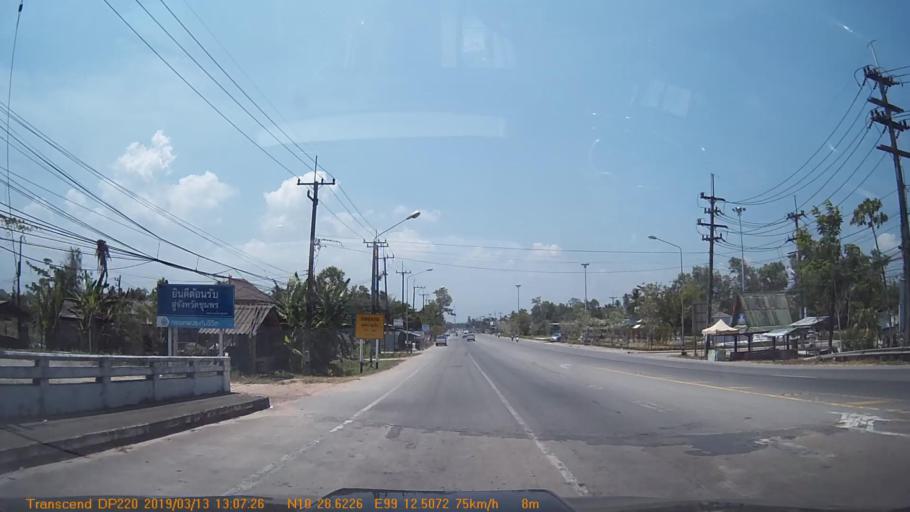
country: TH
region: Chumphon
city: Chumphon
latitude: 10.4773
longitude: 99.2080
